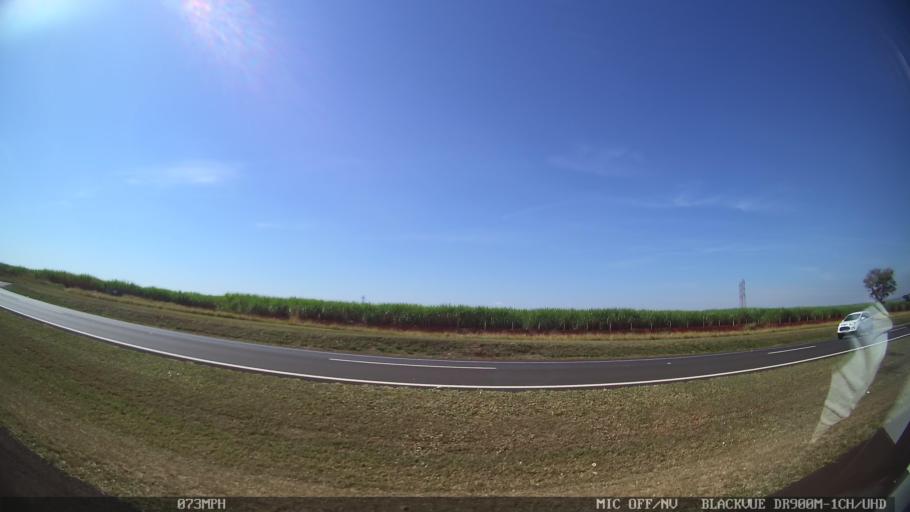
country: BR
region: Sao Paulo
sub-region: Ribeirao Preto
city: Ribeirao Preto
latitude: -21.1841
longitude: -47.8903
